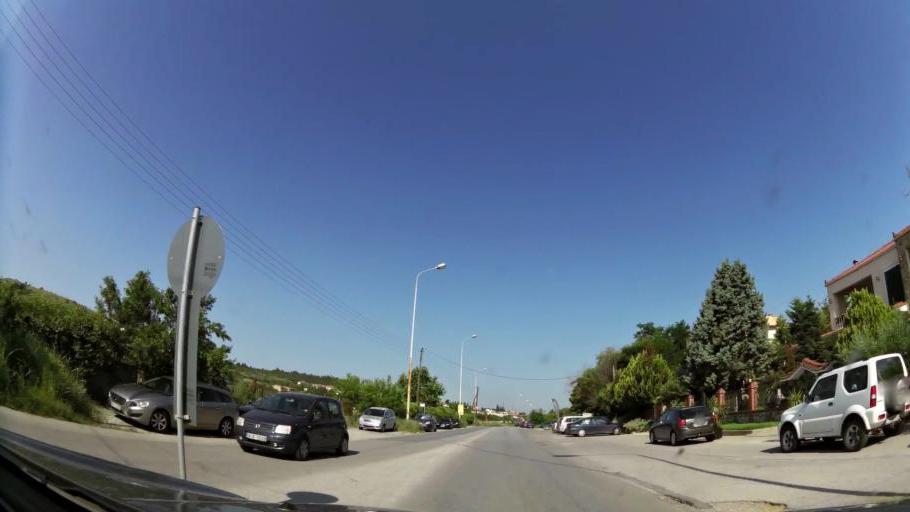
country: GR
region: Central Macedonia
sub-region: Nomos Thessalonikis
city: Neo Rysi
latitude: 40.4959
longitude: 22.9996
